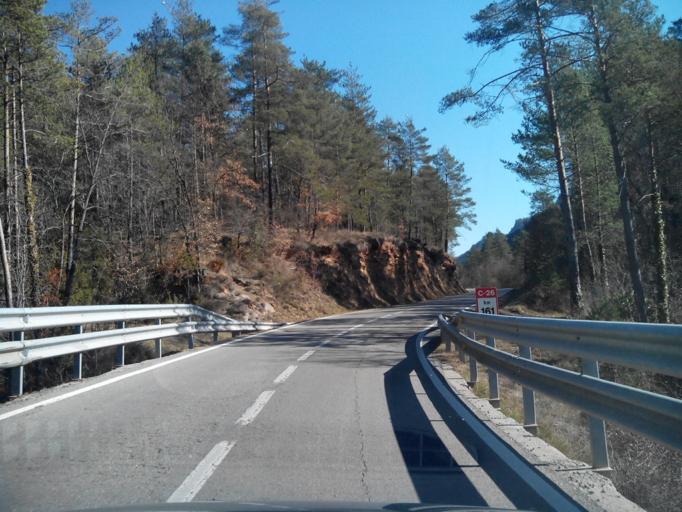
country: ES
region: Catalonia
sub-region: Provincia de Barcelona
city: Vilada
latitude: 42.1300
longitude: 1.9482
